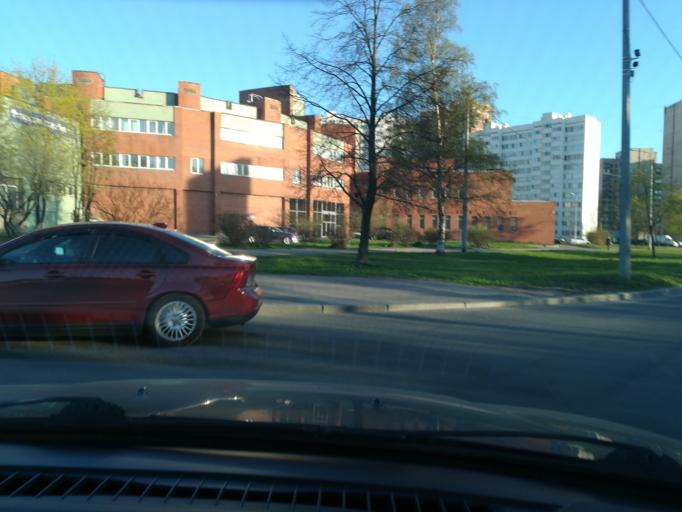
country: RU
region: St.-Petersburg
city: Dachnoye
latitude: 59.8629
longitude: 30.2386
